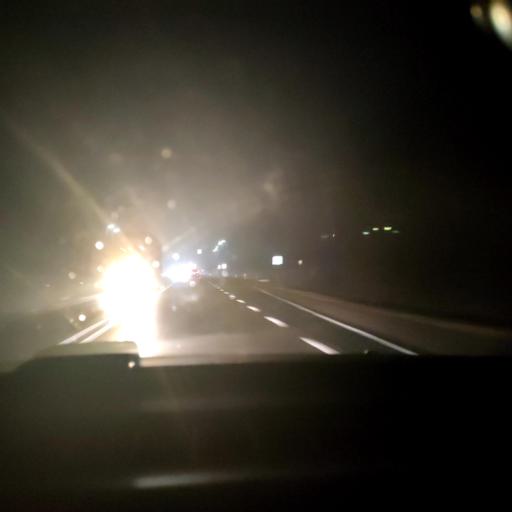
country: RU
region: Voronezj
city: Latnaya
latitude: 51.6489
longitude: 38.7572
